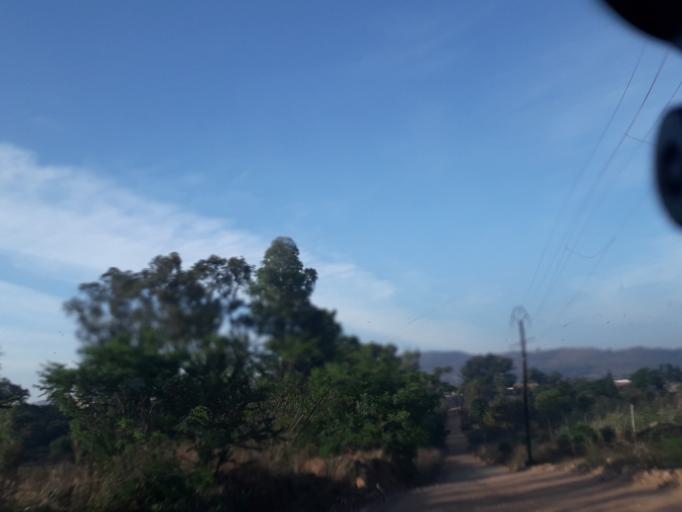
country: ZA
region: Gauteng
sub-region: City of Johannesburg Metropolitan Municipality
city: Roodepoort
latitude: -26.0961
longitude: 27.8964
